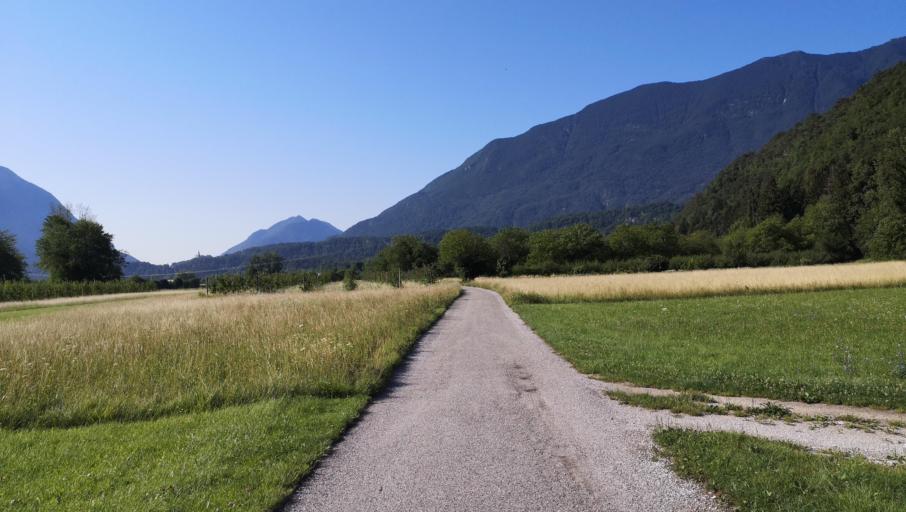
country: IT
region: Friuli Venezia Giulia
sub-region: Provincia di Udine
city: Cavazzo Carnico
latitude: 46.3785
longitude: 13.0405
